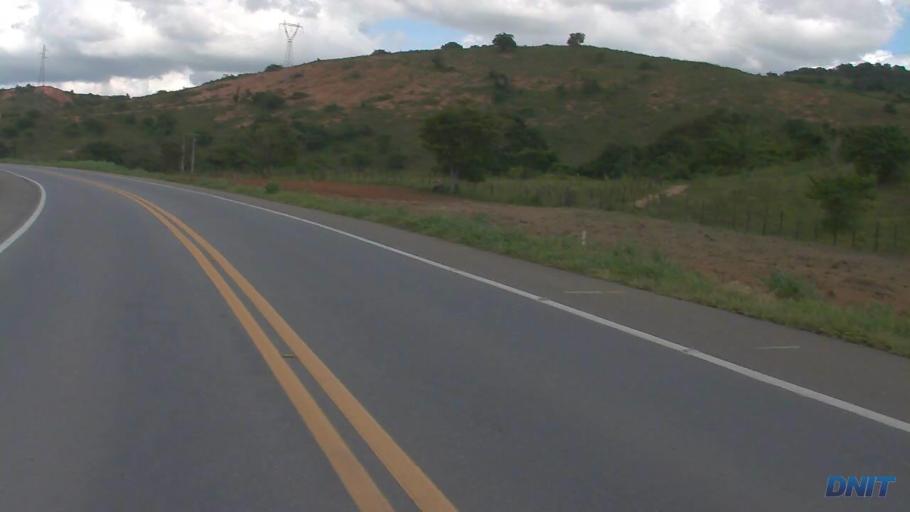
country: BR
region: Minas Gerais
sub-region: Governador Valadares
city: Governador Valadares
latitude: -18.9785
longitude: -42.1000
